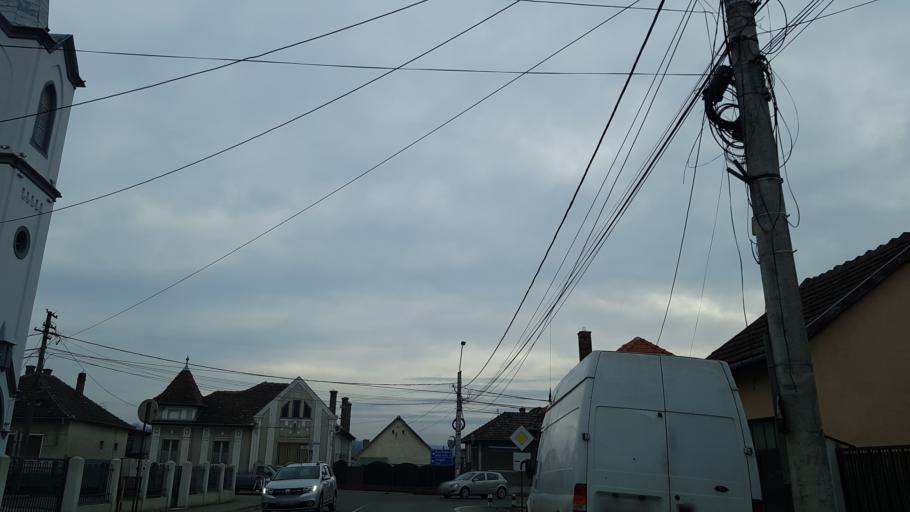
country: RO
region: Alba
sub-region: Municipiul Blaj
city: Blaj
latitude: 46.1761
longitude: 23.9166
